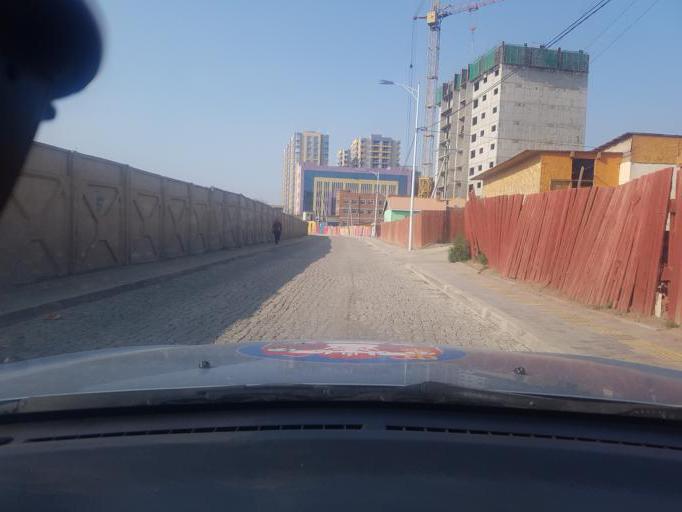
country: MN
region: Ulaanbaatar
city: Ulaanbaatar
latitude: 47.9220
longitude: 106.9665
